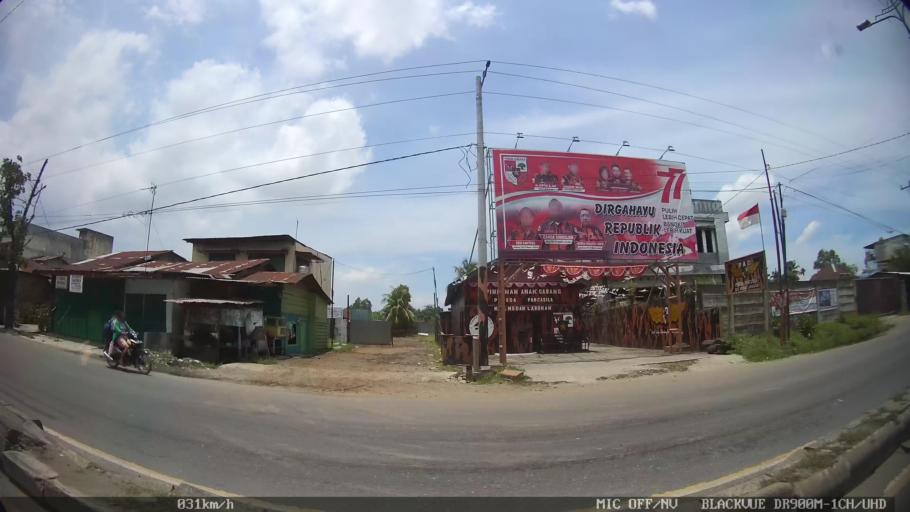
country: ID
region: North Sumatra
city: Labuhan Deli
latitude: 3.7180
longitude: 98.6800
